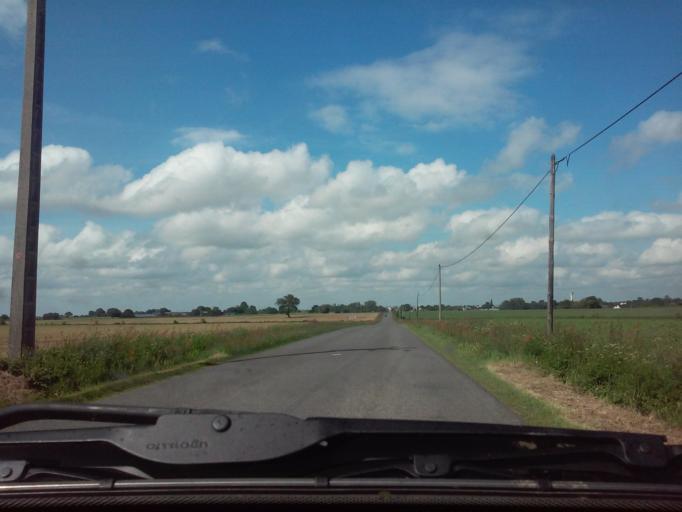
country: FR
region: Pays de la Loire
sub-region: Departement de la Mayenne
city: Quelaines-Saint-Gault
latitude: 47.9050
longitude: -0.8120
